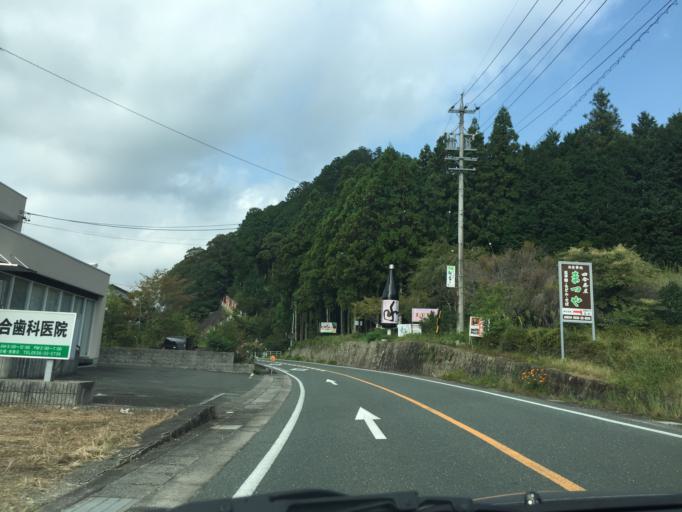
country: JP
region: Aichi
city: Shinshiro
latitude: 34.9632
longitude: 137.6131
